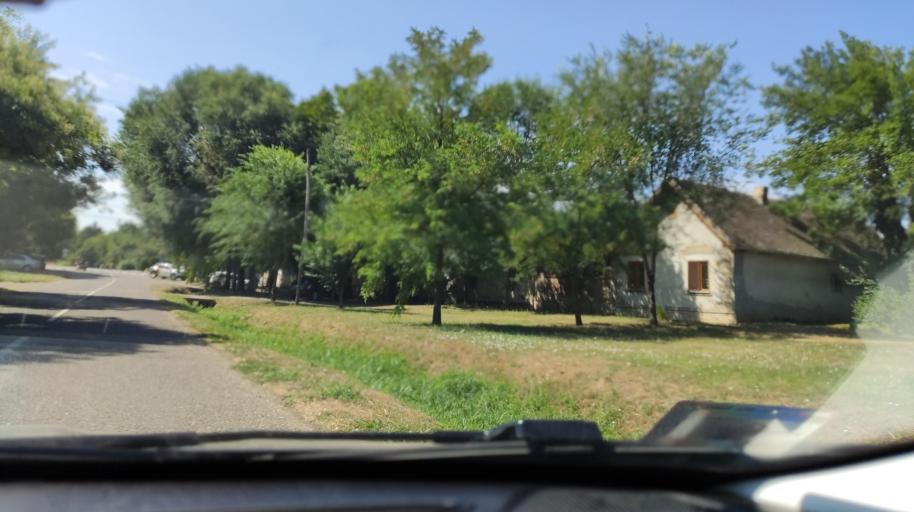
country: RS
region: Autonomna Pokrajina Vojvodina
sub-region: Severnobacki Okrug
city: Backa Topola
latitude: 45.8199
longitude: 19.6221
